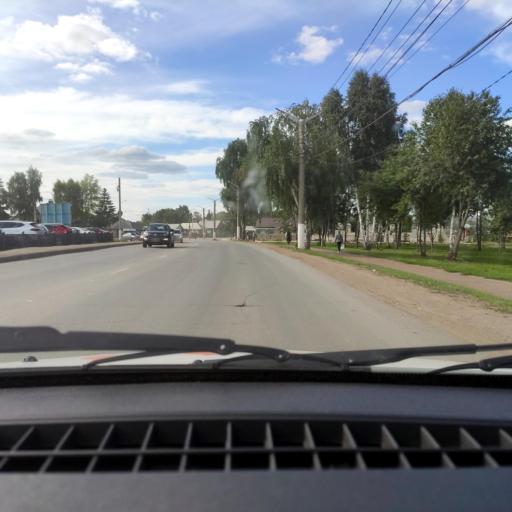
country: RU
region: Bashkortostan
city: Blagoveshchensk
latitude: 55.0335
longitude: 55.9670
